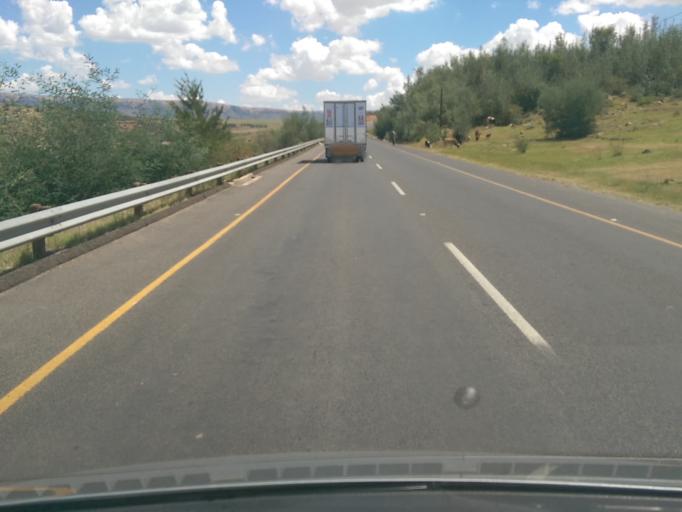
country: LS
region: Maseru
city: Maseru
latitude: -29.3986
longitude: 27.5342
